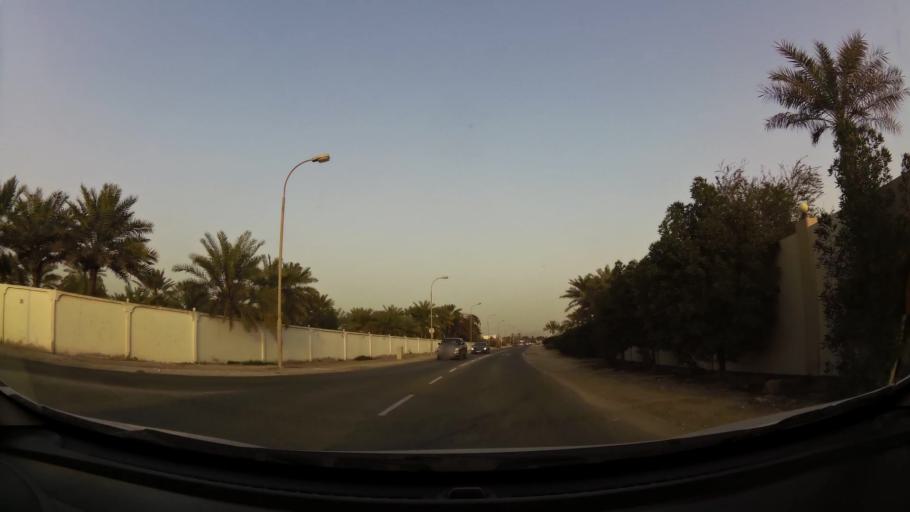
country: BH
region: Manama
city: Jidd Hafs
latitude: 26.1970
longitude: 50.4736
